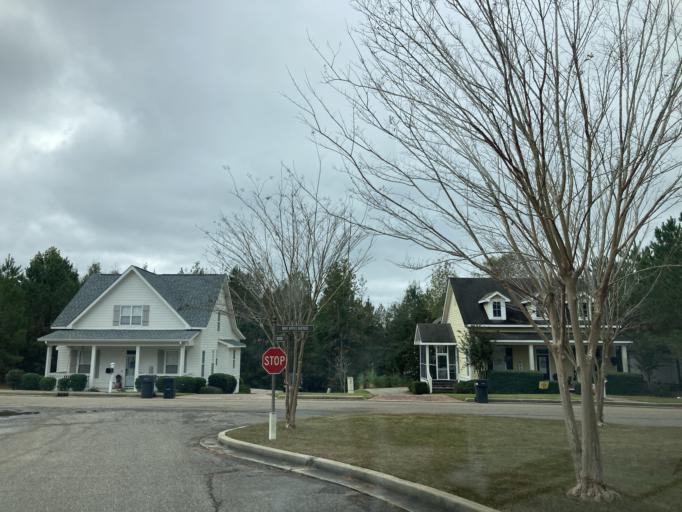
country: US
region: Mississippi
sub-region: Lamar County
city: West Hattiesburg
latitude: 31.2837
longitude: -89.4740
